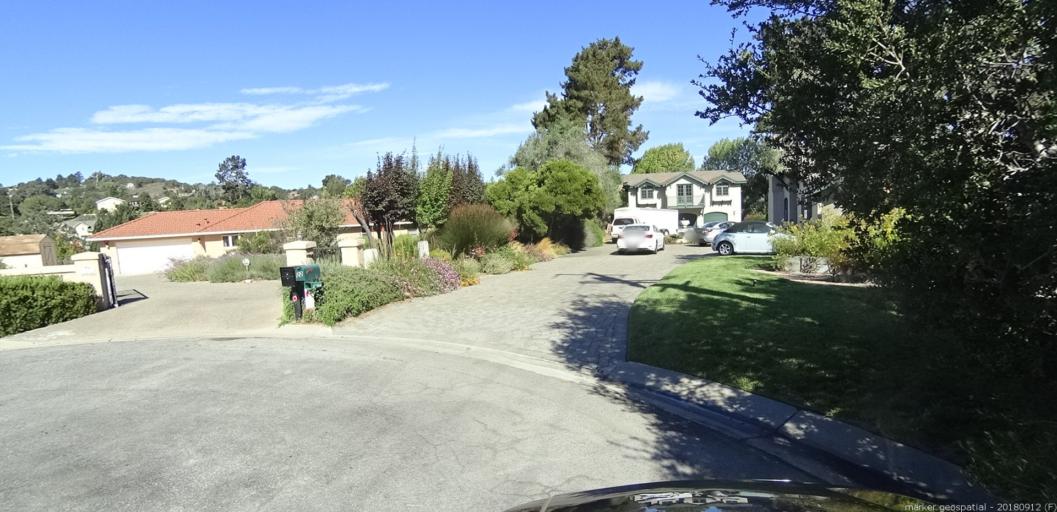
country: US
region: California
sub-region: Monterey County
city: Carmel Valley Village
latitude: 36.5700
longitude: -121.7293
